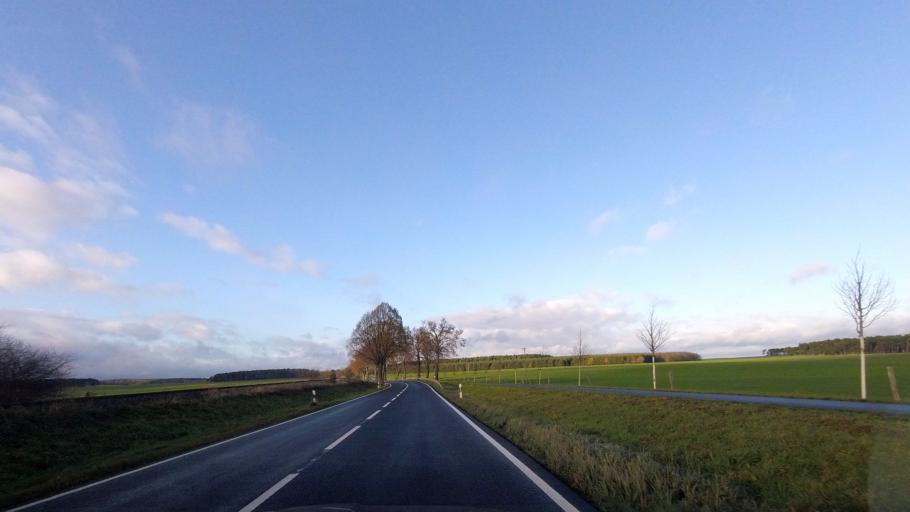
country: DE
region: Brandenburg
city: Niemegk
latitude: 52.1128
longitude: 12.6475
